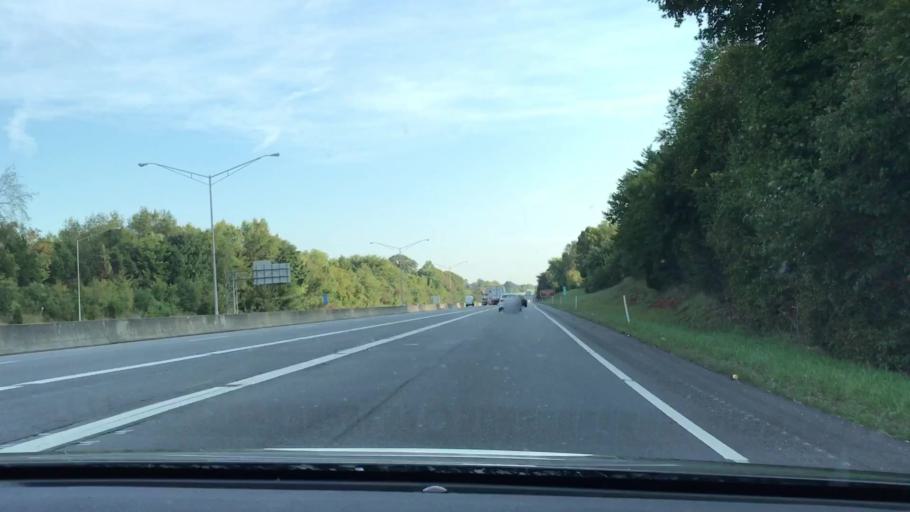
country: US
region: Kentucky
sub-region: Warren County
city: Bowling Green
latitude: 36.9804
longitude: -86.3893
